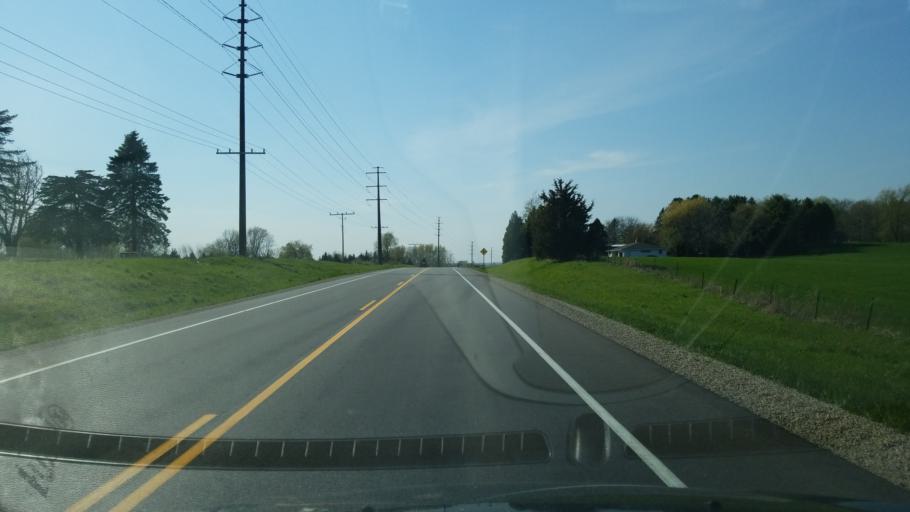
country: US
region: Wisconsin
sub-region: Dane County
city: Fitchburg
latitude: 42.9662
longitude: -89.4916
